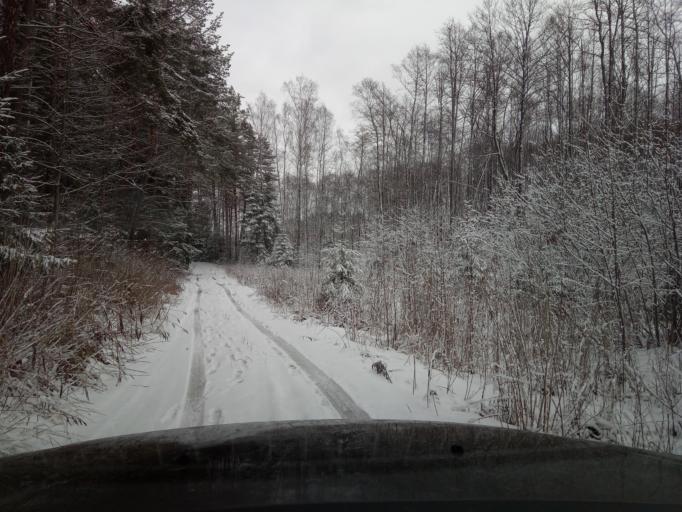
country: LT
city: Zarasai
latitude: 55.6736
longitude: 26.0238
